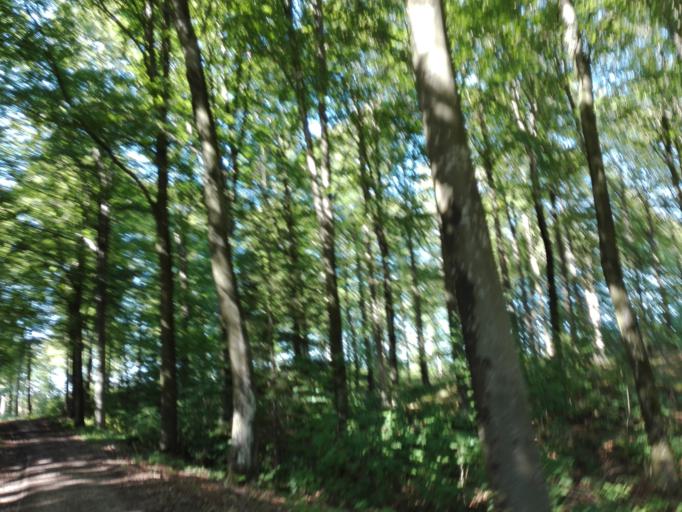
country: DK
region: Central Jutland
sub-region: Odder Kommune
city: Odder
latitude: 55.9702
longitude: 10.1249
